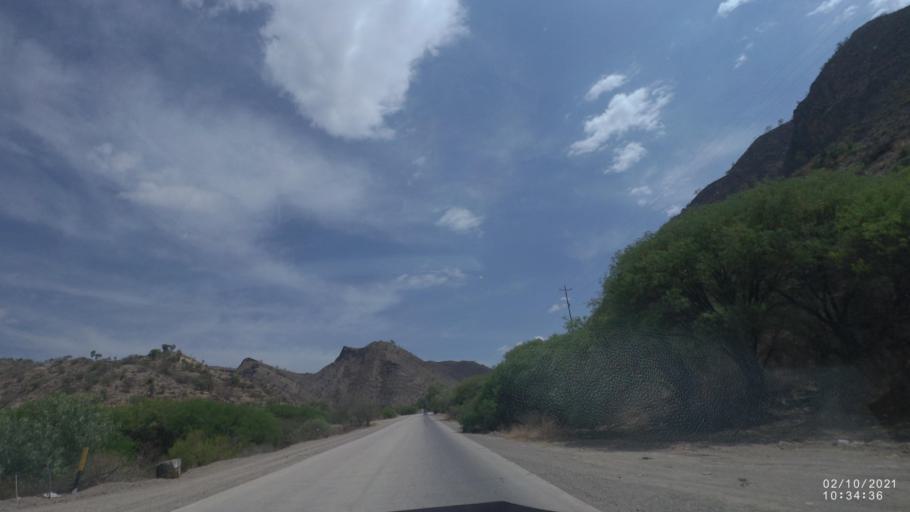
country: BO
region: Cochabamba
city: Capinota
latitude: -17.6715
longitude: -66.2560
